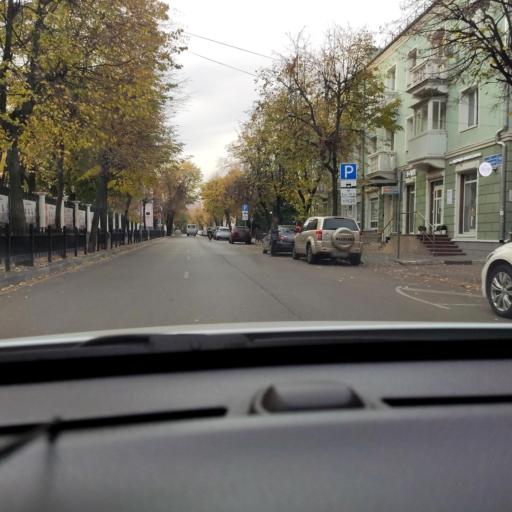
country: RU
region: Voronezj
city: Voronezh
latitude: 51.6707
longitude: 39.2034
